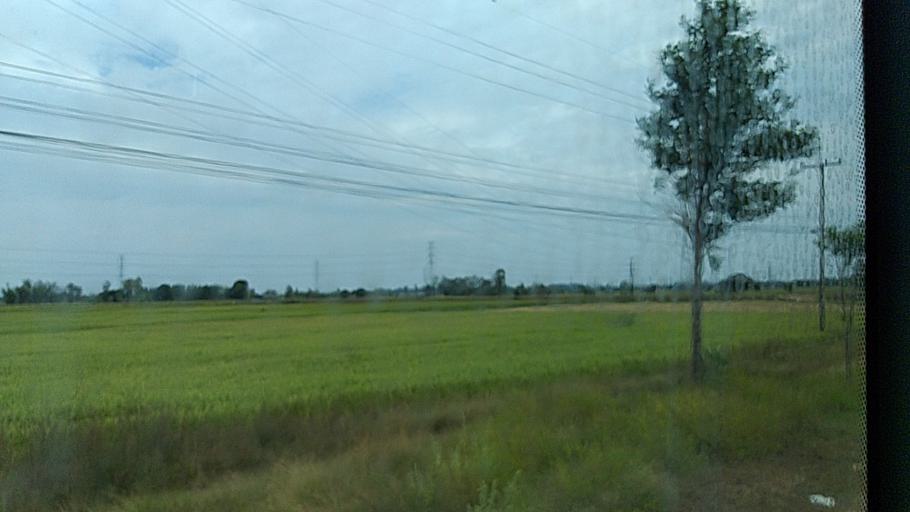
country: TH
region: Roi Et
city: Si Somdet
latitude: 16.1265
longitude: 103.4729
